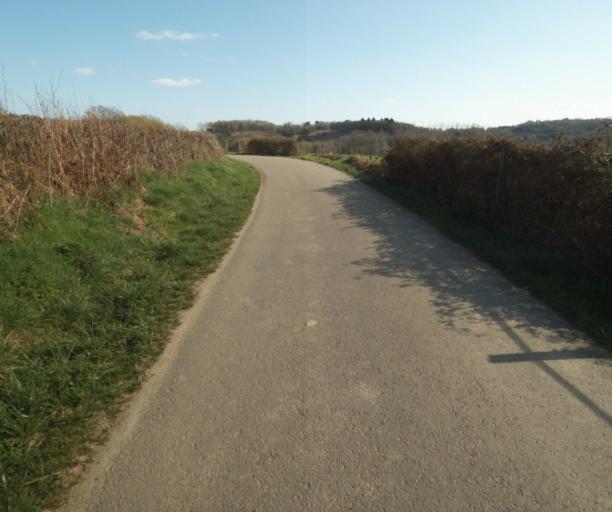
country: FR
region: Limousin
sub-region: Departement de la Correze
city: Saint-Mexant
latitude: 45.3254
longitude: 1.6148
